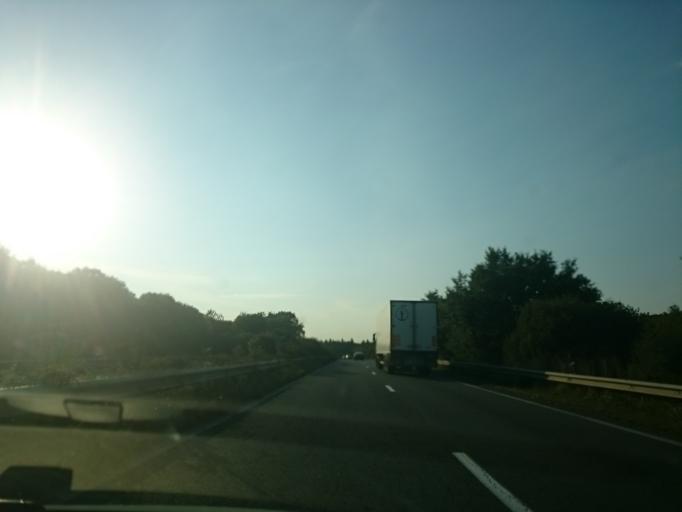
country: FR
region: Pays de la Loire
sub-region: Departement de la Loire-Atlantique
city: Missillac
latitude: 47.4844
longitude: -2.1994
